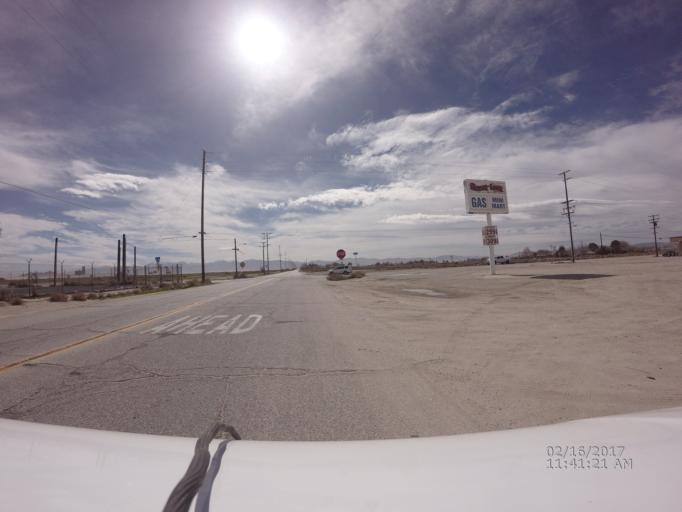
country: US
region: California
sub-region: Los Angeles County
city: Lake Los Angeles
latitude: 34.6907
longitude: -117.9698
